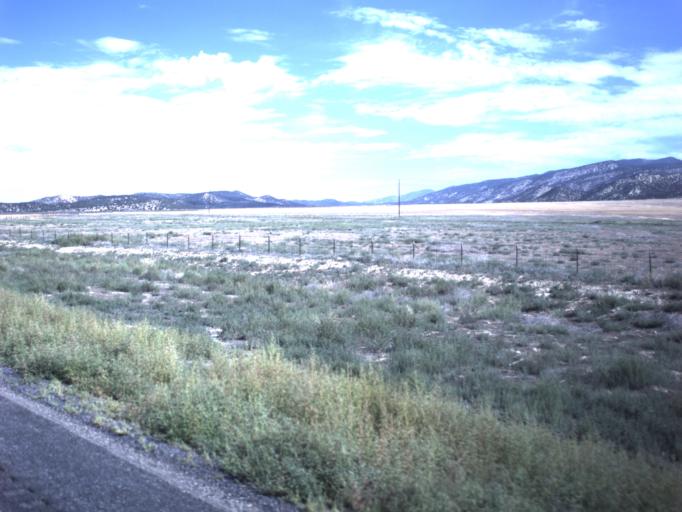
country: US
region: Utah
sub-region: Sanpete County
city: Gunnison
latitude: 39.3034
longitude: -111.8954
